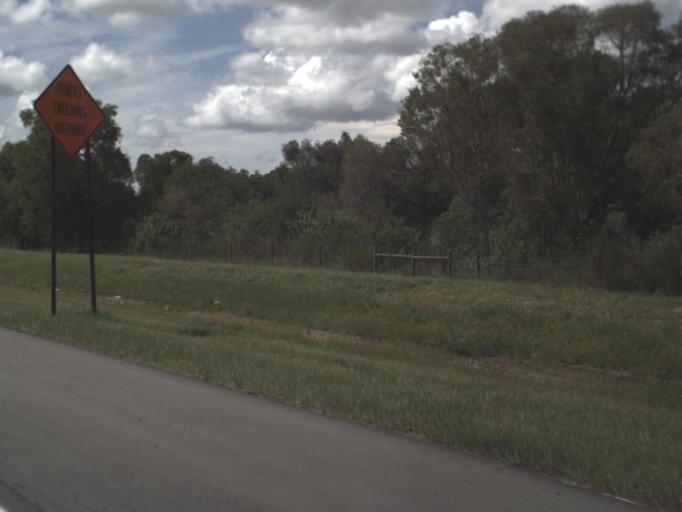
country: US
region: Florida
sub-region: Lee County
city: Gateway
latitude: 26.5346
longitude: -81.7951
